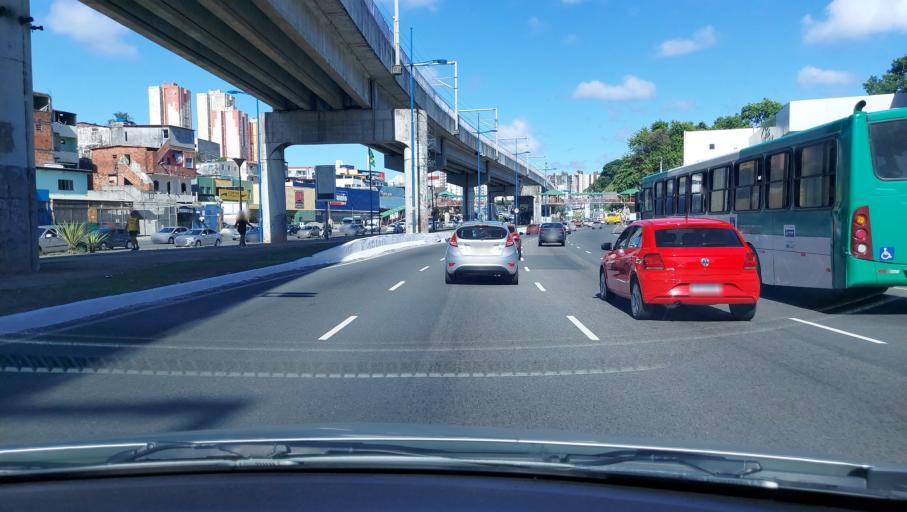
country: BR
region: Bahia
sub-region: Salvador
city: Salvador
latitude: -12.9842
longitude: -38.4898
